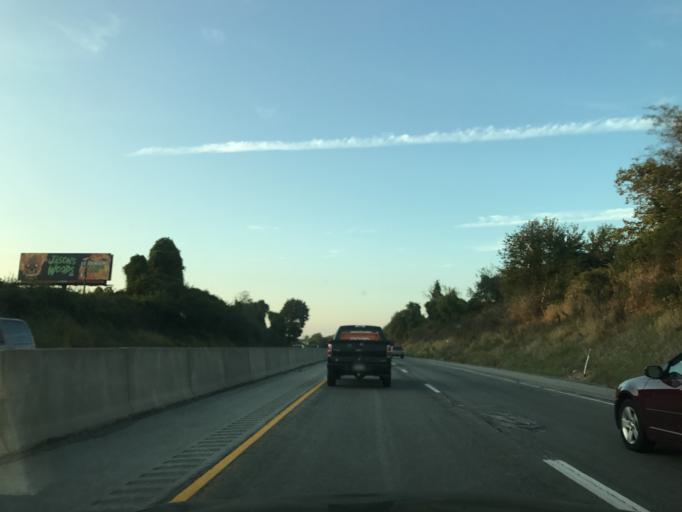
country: US
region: Pennsylvania
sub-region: York County
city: Shrewsbury
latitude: 39.8115
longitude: -76.6801
